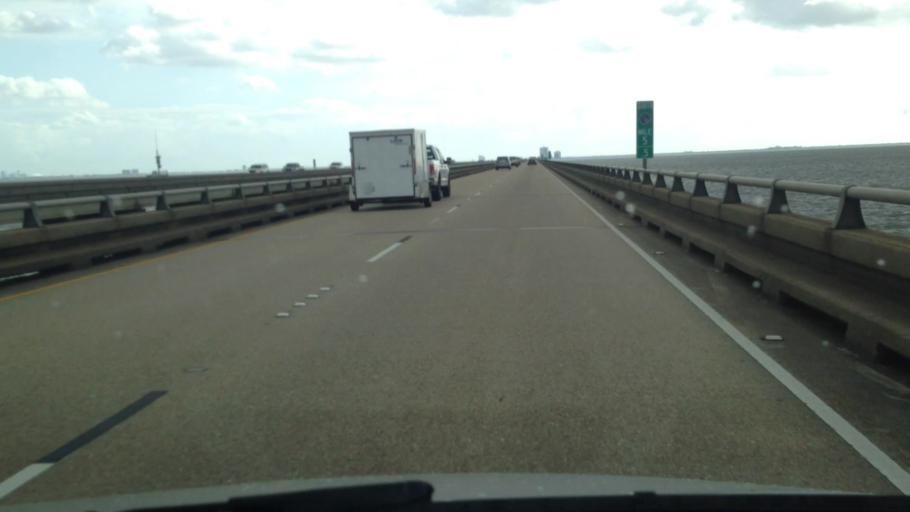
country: US
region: Louisiana
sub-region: Jefferson Parish
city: Metairie
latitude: 30.1012
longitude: -90.1402
